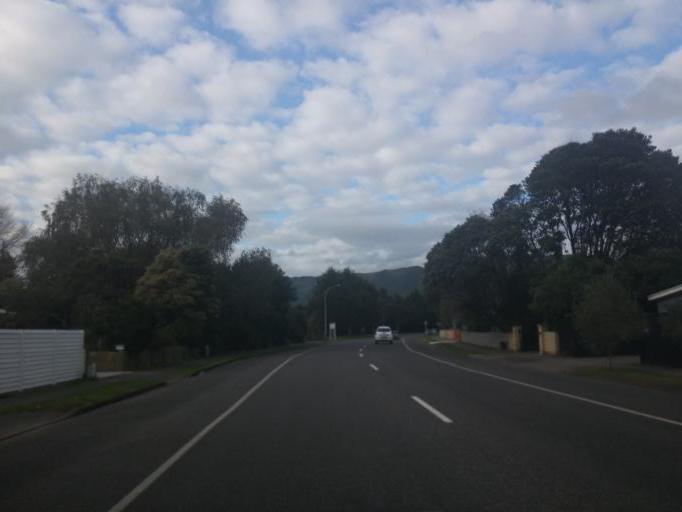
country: NZ
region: Wellington
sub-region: Kapiti Coast District
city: Paraparaumu
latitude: -40.8714
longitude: 175.0416
